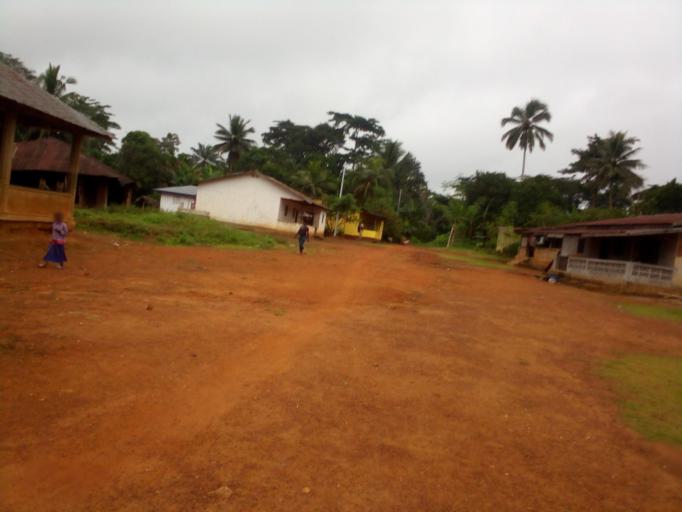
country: SL
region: Eastern Province
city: Kailahun
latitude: 8.2502
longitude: -10.6078
